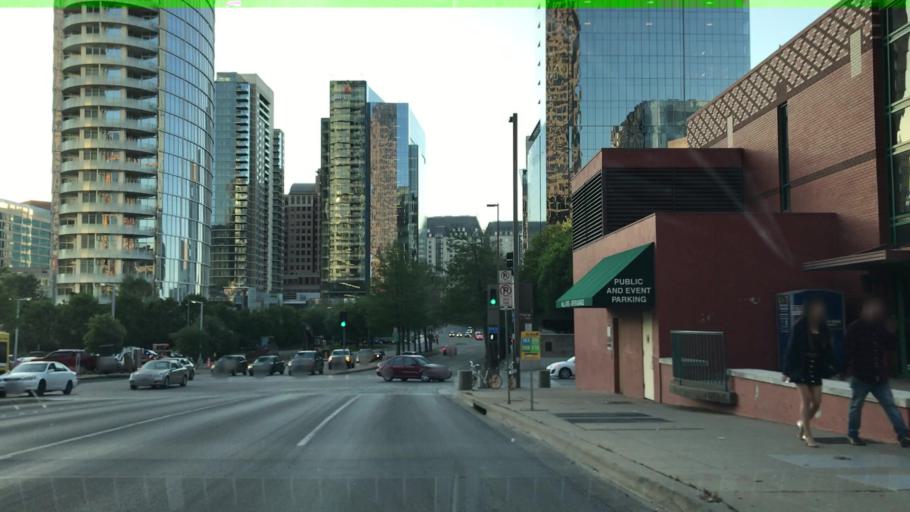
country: US
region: Texas
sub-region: Dallas County
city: Dallas
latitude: 32.7887
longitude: -96.7984
